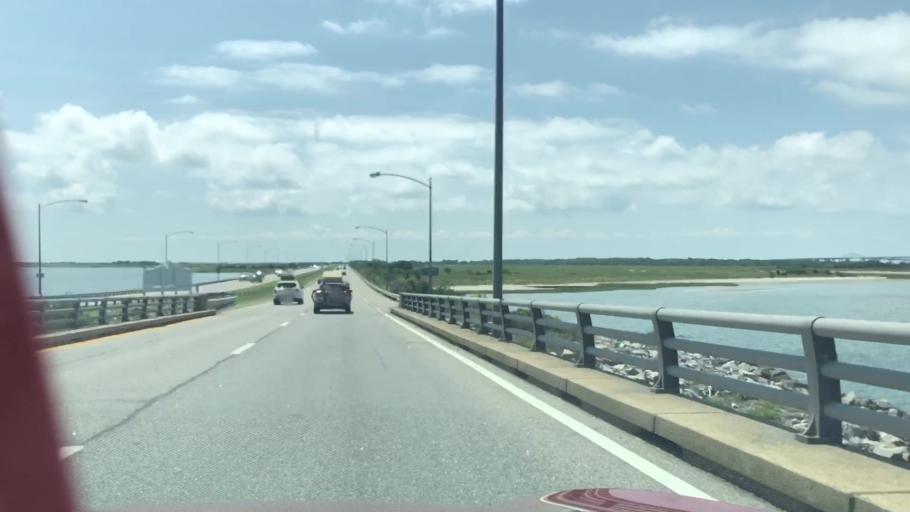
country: US
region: Virginia
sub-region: Northampton County
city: Cape Charles
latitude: 37.1126
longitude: -75.9694
